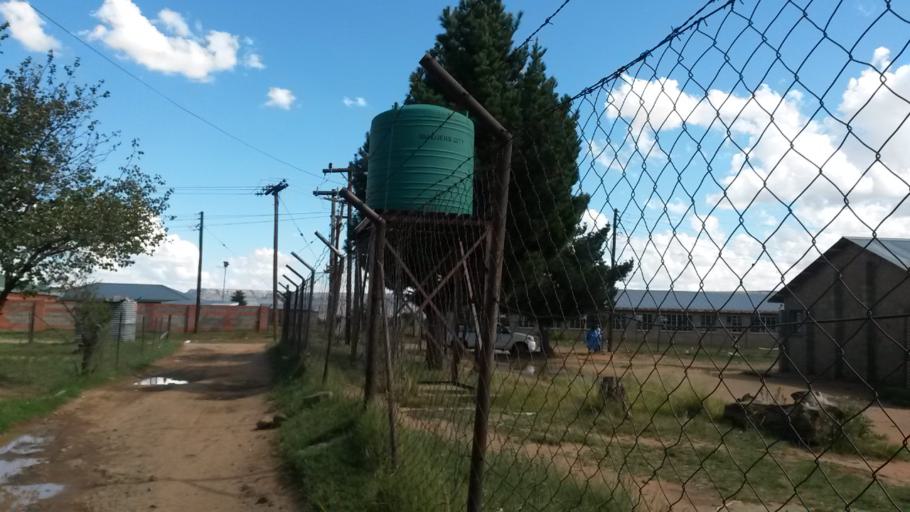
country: LS
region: Maseru
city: Maseru
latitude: -29.3720
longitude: 27.5096
